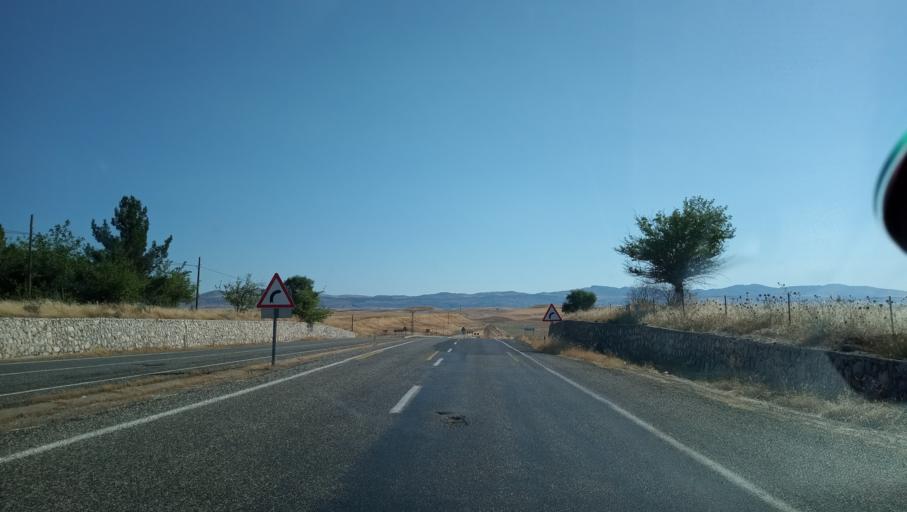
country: TR
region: Diyarbakir
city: Bagdere
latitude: 38.1216
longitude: 40.7418
